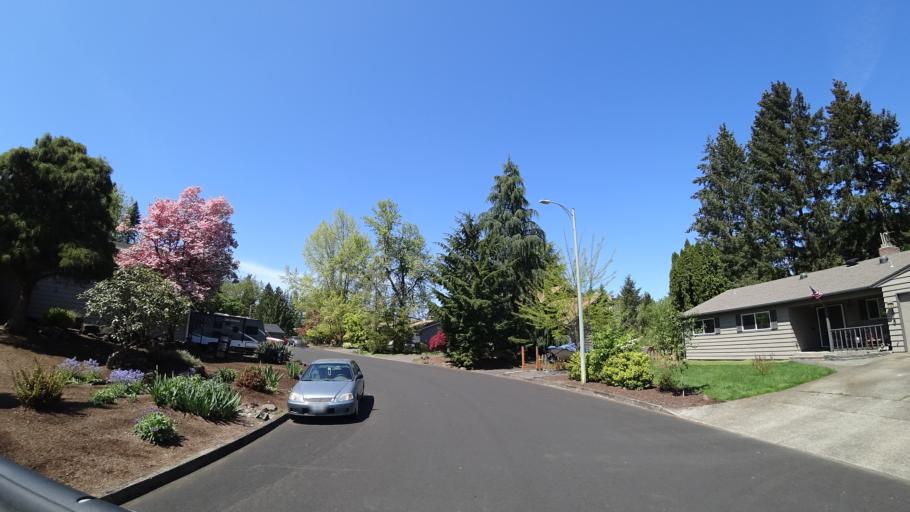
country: US
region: Oregon
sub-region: Washington County
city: Hillsboro
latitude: 45.5178
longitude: -122.9621
